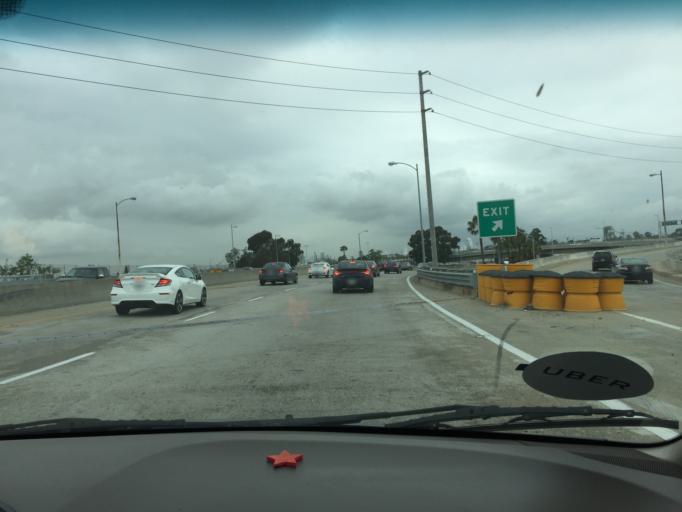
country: US
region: California
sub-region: Los Angeles County
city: Long Beach
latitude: 33.7776
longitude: -118.2063
